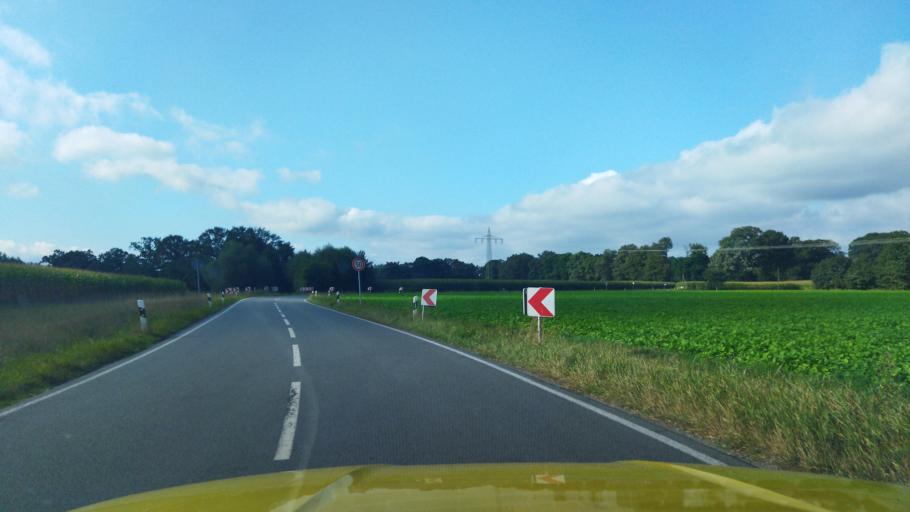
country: DE
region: North Rhine-Westphalia
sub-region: Regierungsbezirk Munster
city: Ostbevern
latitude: 52.1152
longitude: 7.8775
